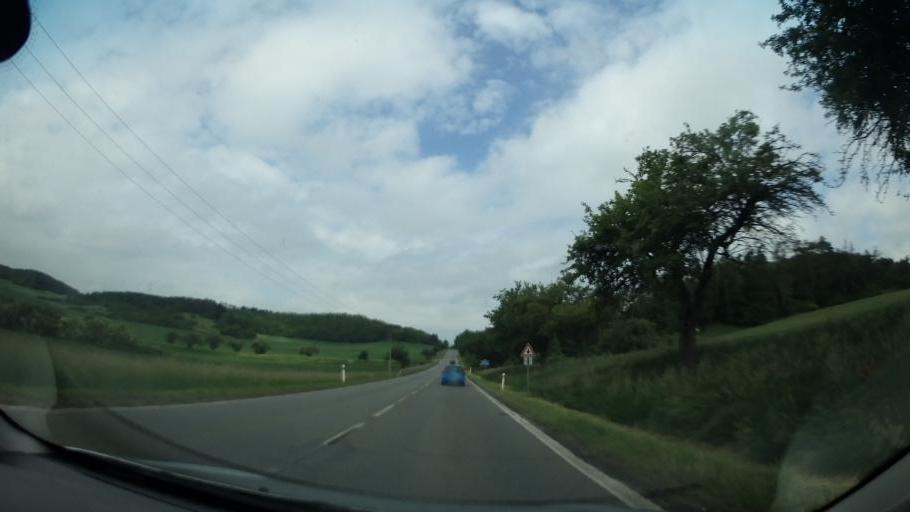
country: CZ
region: South Moravian
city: Kurim
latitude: 49.3064
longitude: 16.5062
